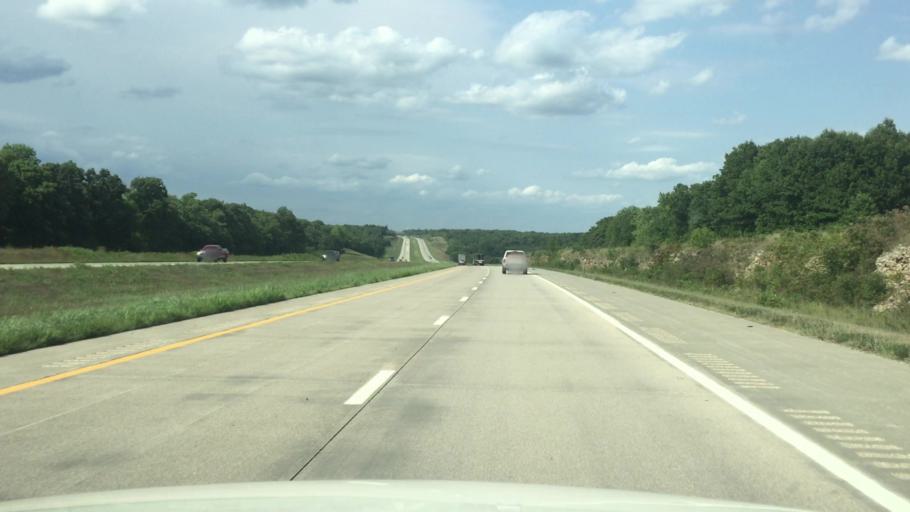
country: US
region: Kansas
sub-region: Miami County
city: Louisburg
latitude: 38.5874
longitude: -94.6942
